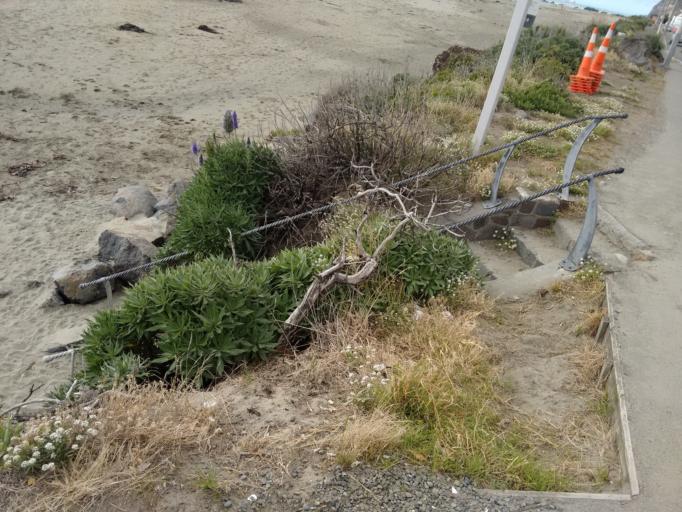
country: NZ
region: Canterbury
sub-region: Christchurch City
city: Christchurch
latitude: -43.5637
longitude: 172.7498
